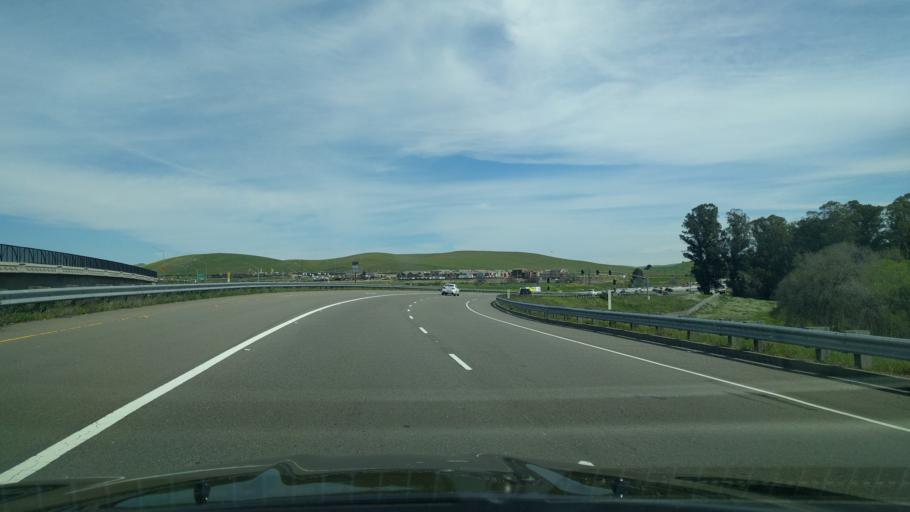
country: US
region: California
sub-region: Alameda County
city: Livermore
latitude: 37.6998
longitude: -121.8027
